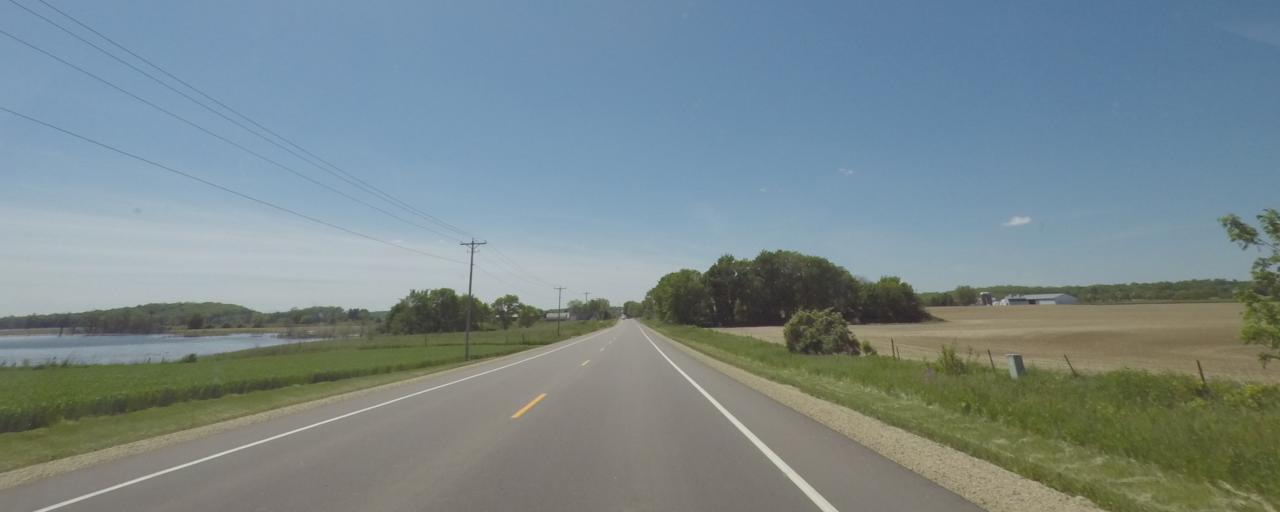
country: US
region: Wisconsin
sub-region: Dane County
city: Oregon
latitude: 42.9504
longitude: -89.4059
